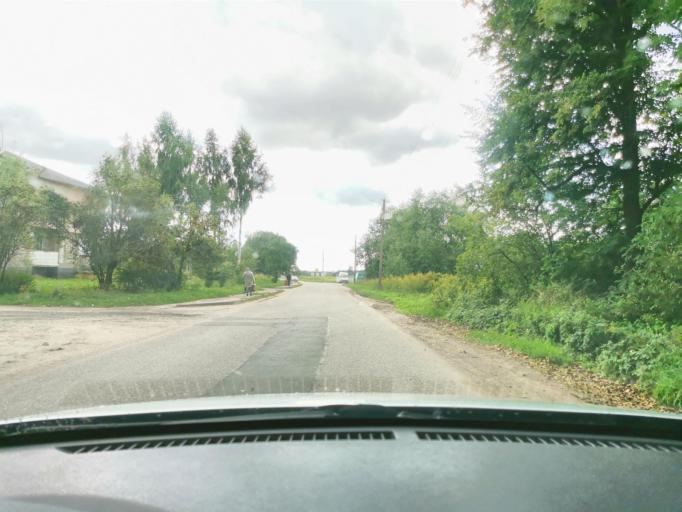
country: RU
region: Kaliningrad
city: Chernyakhovsk
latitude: 54.6584
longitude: 21.8303
